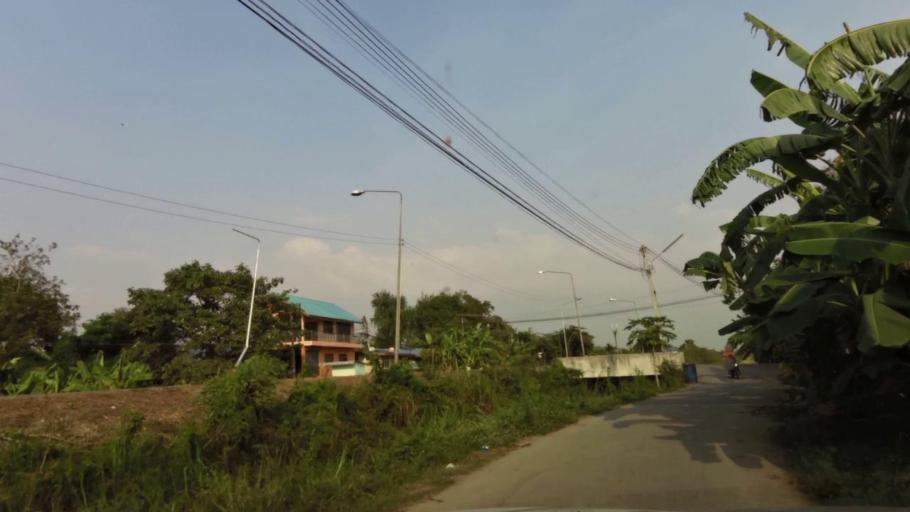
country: TH
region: Phra Nakhon Si Ayutthaya
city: Phra Nakhon Si Ayutthaya
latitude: 14.3345
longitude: 100.5647
